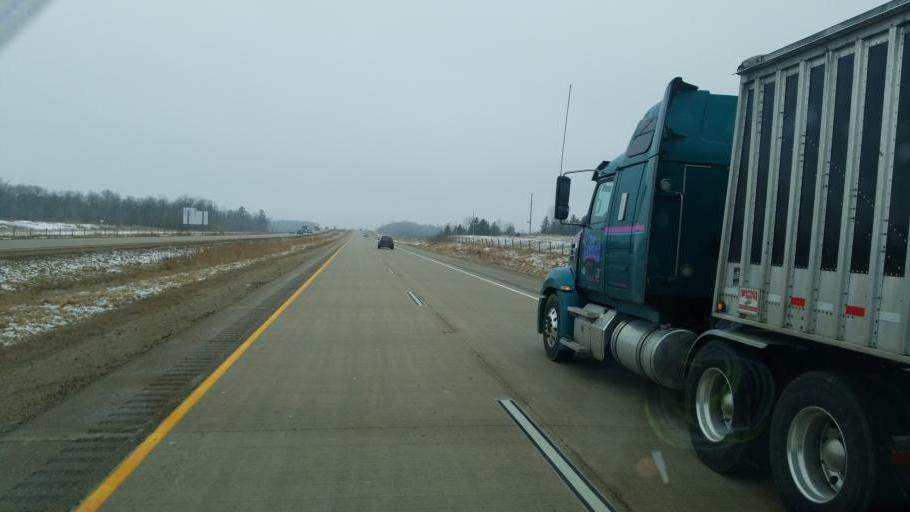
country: US
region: Wisconsin
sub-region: Winnebago County
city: Winneconne
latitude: 44.2343
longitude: -88.7558
